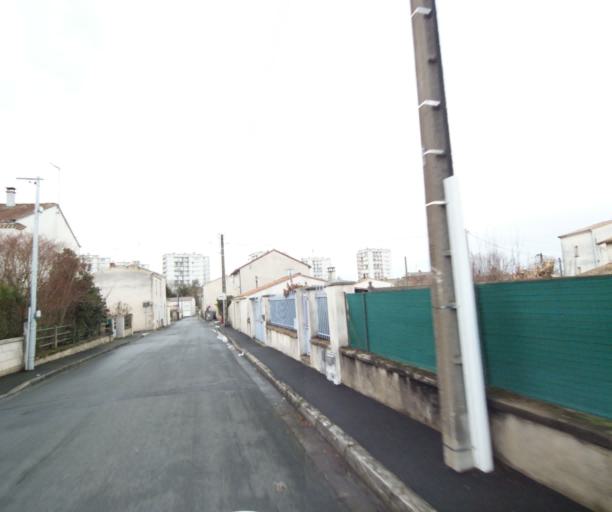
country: FR
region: Poitou-Charentes
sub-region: Departement des Deux-Sevres
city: Niort
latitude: 46.3327
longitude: -0.4538
